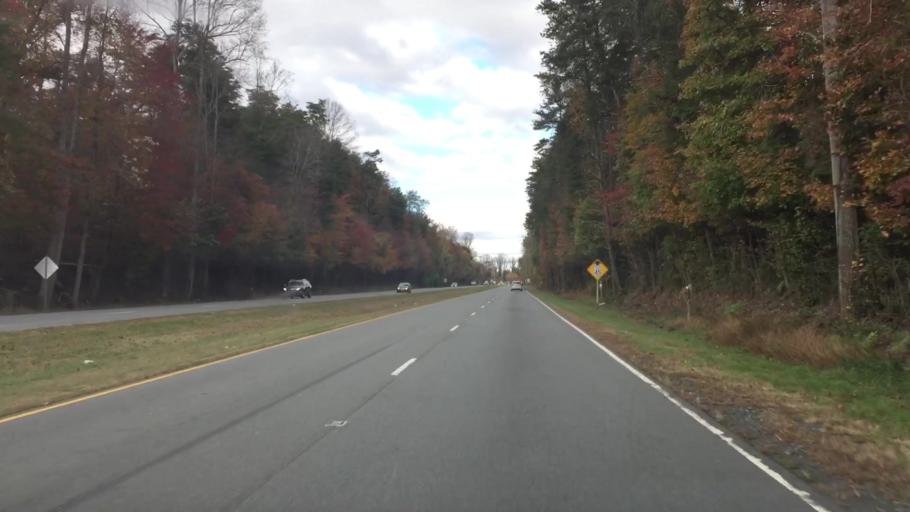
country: US
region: North Carolina
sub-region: Forsyth County
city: Winston-Salem
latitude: 36.1088
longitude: -80.1901
